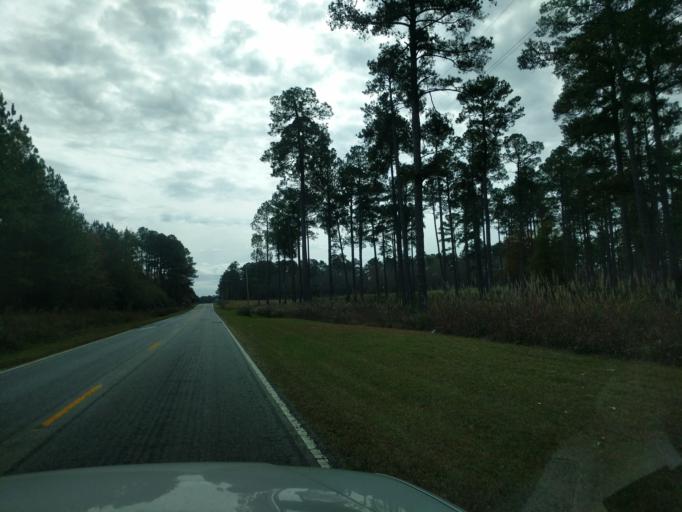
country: US
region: South Carolina
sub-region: Laurens County
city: Joanna
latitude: 34.3258
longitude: -81.8494
